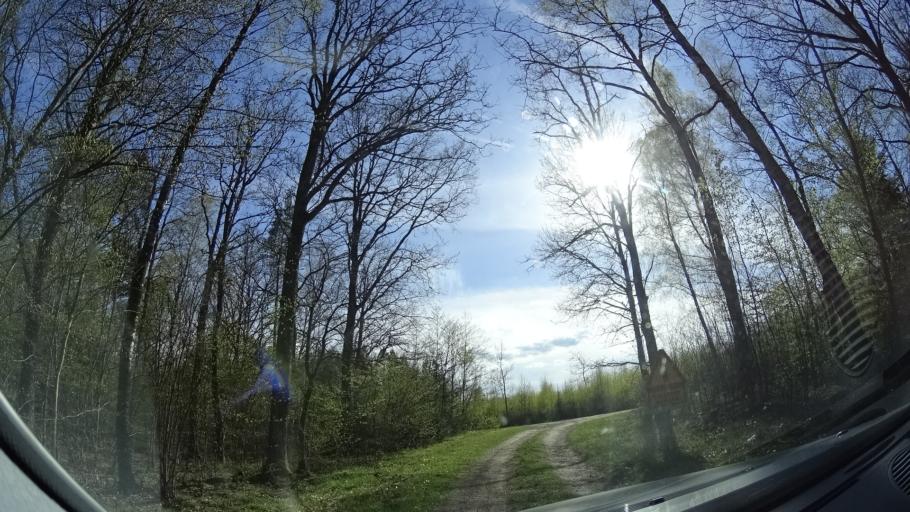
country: SE
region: Skane
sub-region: Hassleholms Kommun
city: Tormestorp
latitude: 56.0987
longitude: 13.6712
